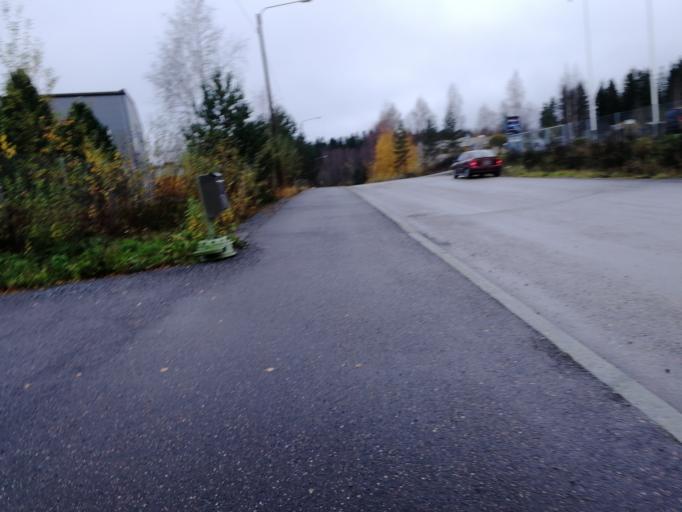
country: FI
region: Pirkanmaa
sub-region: Tampere
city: Tampere
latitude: 61.4552
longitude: 23.8845
